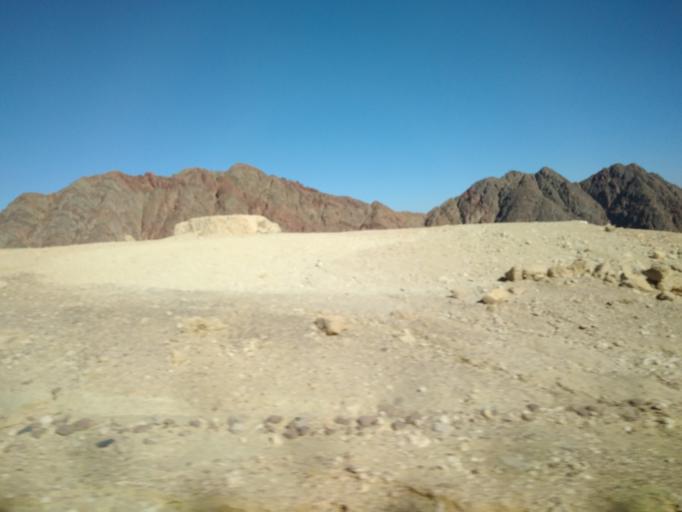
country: IL
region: Southern District
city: Eilat
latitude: 29.5771
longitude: 34.8865
